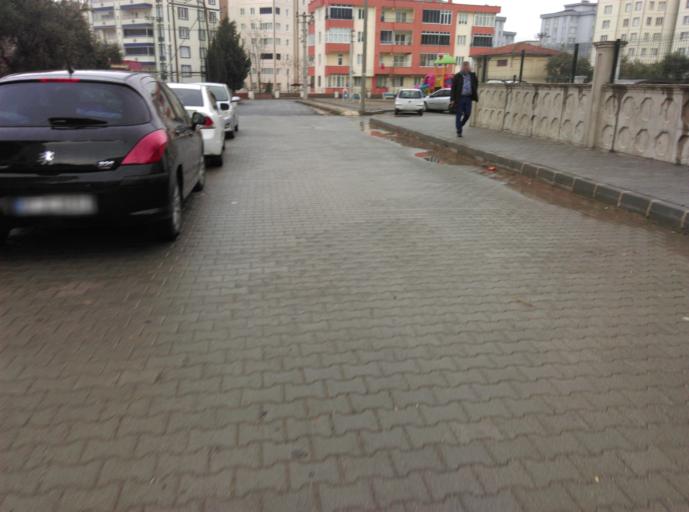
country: TR
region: Kahramanmaras
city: Kahramanmaras
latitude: 37.5826
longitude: 36.8949
